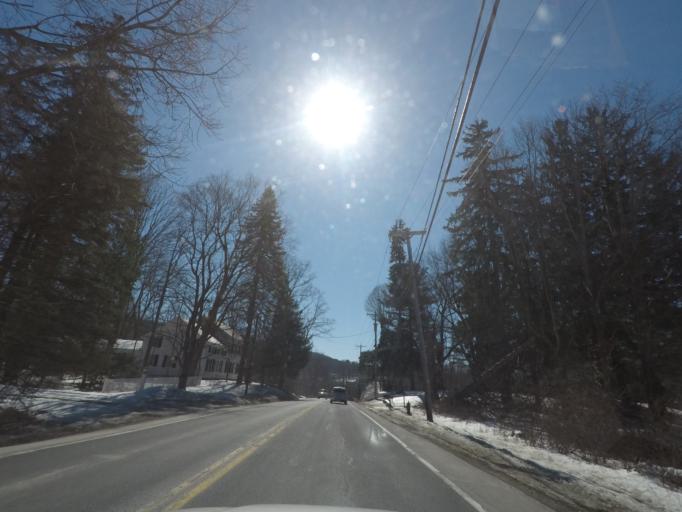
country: US
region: New York
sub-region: Saratoga County
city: Waterford
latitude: 42.8331
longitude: -73.6256
